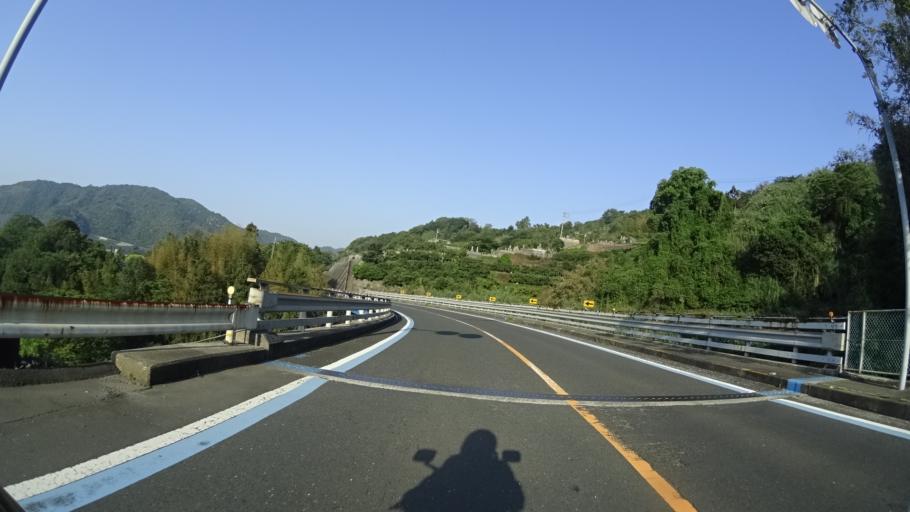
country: JP
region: Ehime
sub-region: Nishiuwa-gun
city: Ikata-cho
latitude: 33.4915
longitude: 132.3532
